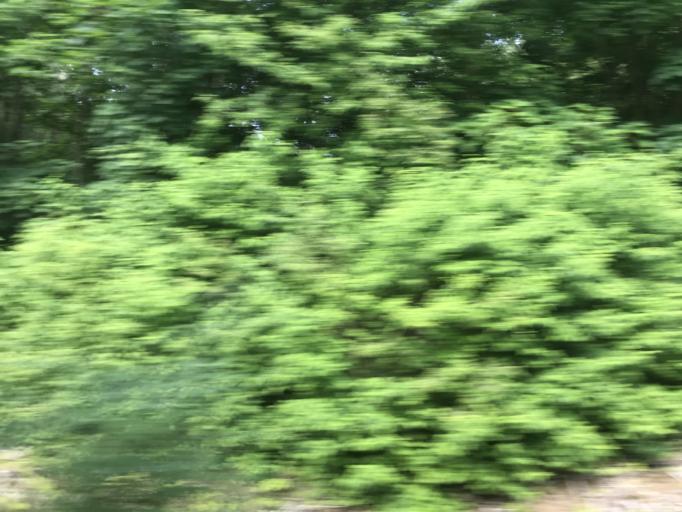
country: FR
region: Ile-de-France
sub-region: Departement de Seine-Saint-Denis
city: Villepinte
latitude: 48.9644
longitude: 2.5115
